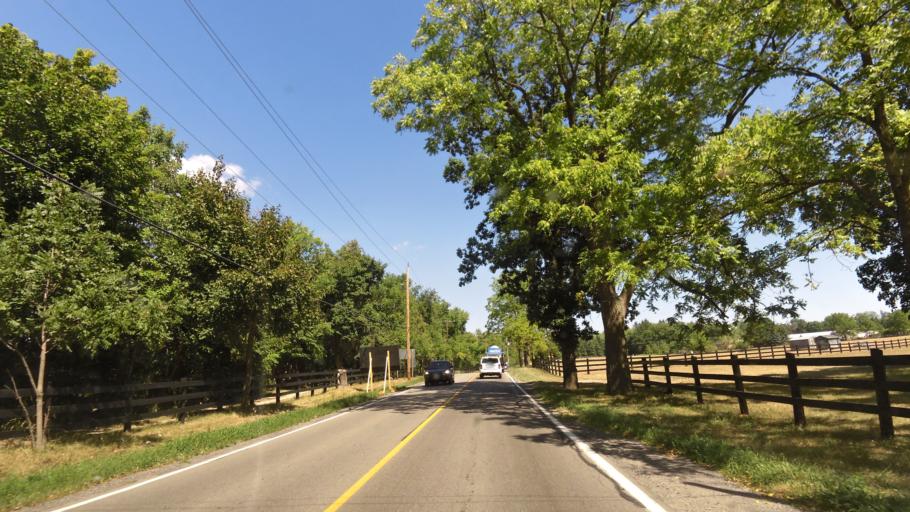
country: CA
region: Ontario
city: Brampton
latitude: 43.6432
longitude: -79.8499
